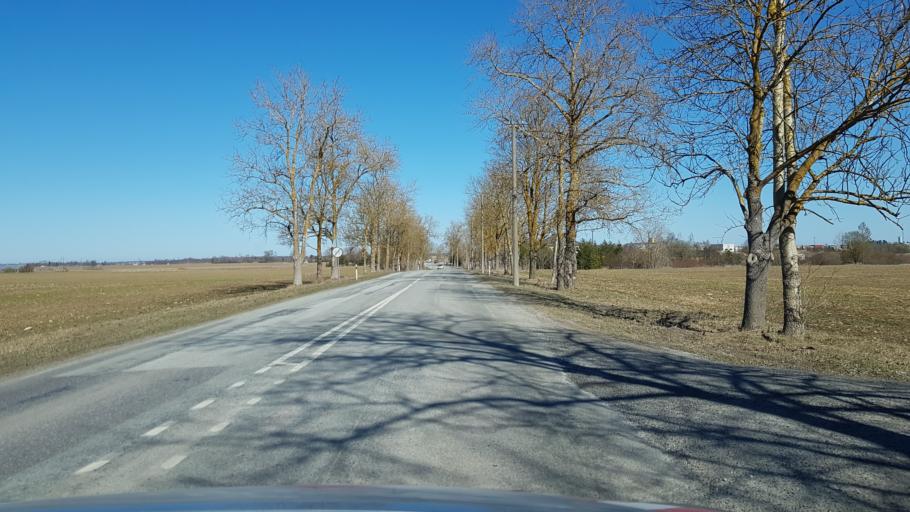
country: EE
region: Laeaene-Virumaa
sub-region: Rakvere linn
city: Rakvere
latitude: 59.3666
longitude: 26.3731
